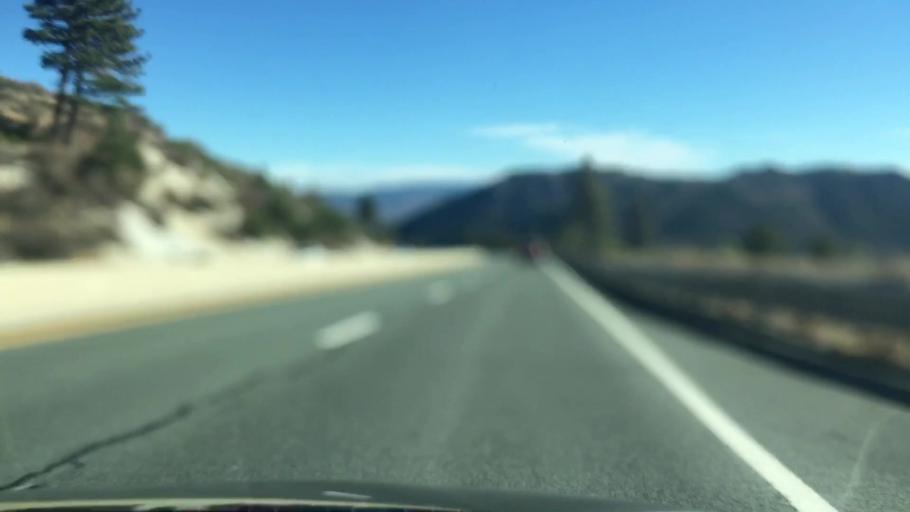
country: US
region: Nevada
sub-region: Douglas County
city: Indian Hills
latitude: 39.1166
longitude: -119.8535
